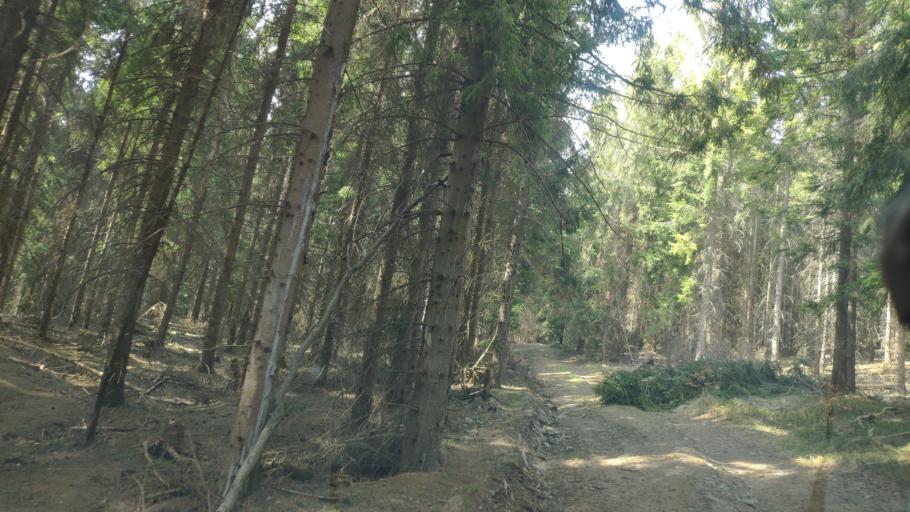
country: SK
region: Kosicky
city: Gelnica
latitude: 48.7586
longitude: 21.0187
